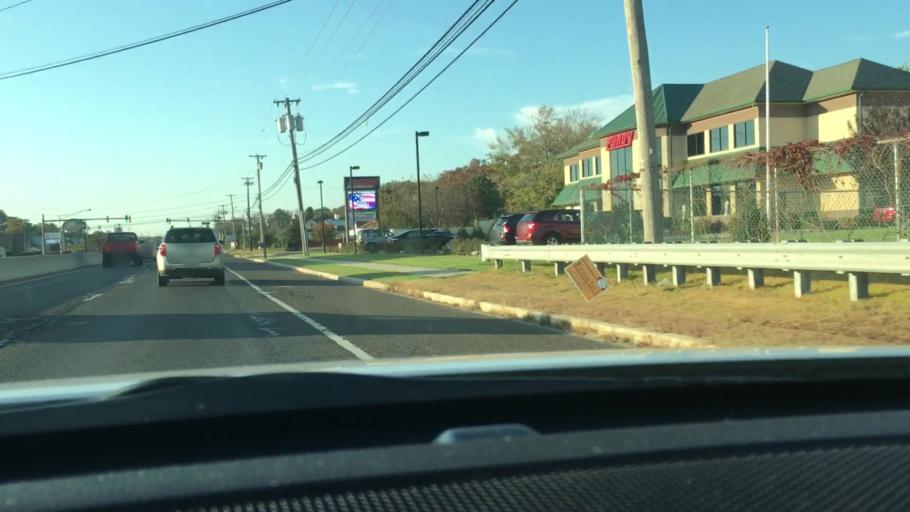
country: US
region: New Jersey
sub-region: Atlantic County
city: Absecon
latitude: 39.4419
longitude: -74.5222
